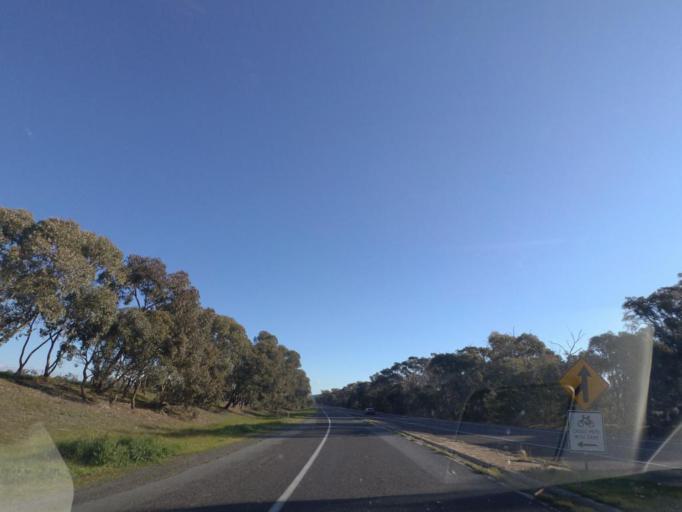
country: AU
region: Victoria
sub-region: Greater Shepparton
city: Shepparton
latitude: -36.7824
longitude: 145.4993
